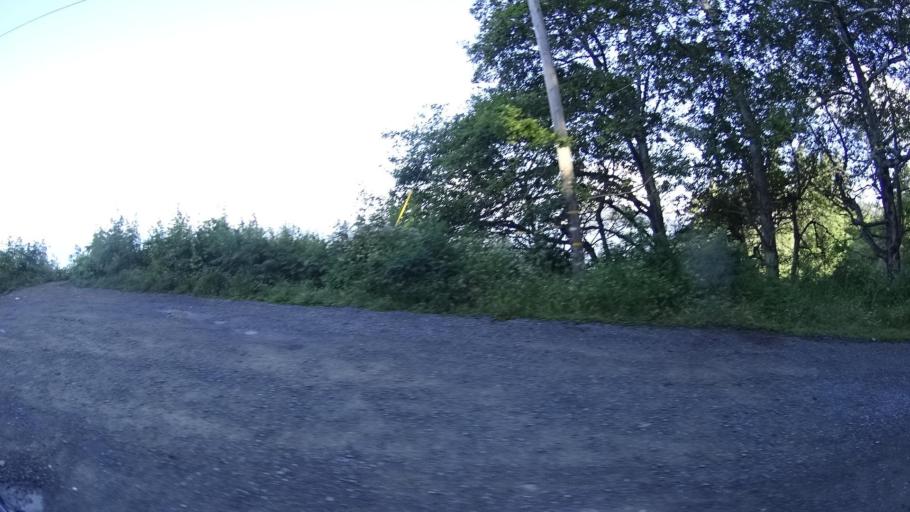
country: US
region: California
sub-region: Humboldt County
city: Westhaven-Moonstone
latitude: 41.0460
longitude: -124.1234
